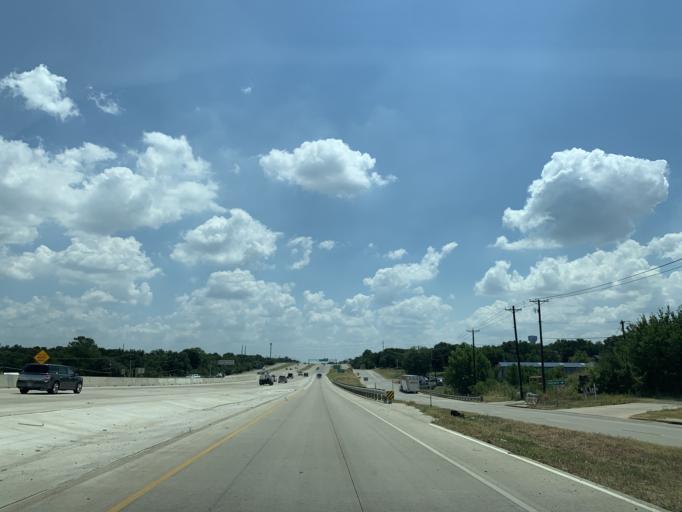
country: US
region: Texas
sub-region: Tarrant County
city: Lakeside
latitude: 32.8354
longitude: -97.4895
